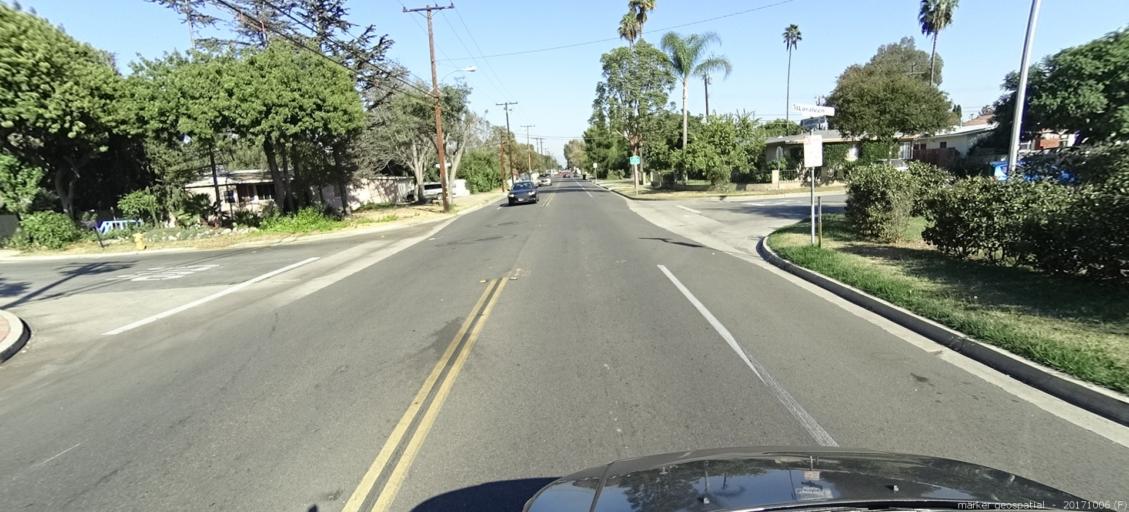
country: US
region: California
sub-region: Orange County
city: Stanton
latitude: 33.7812
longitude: -117.9712
